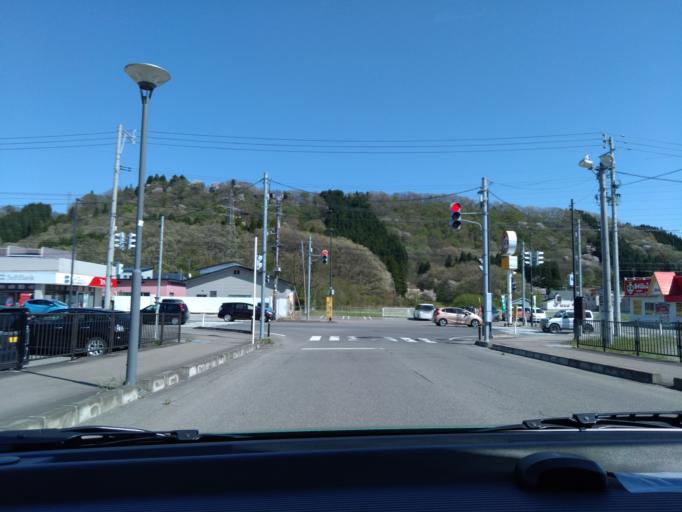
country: JP
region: Akita
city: Kakunodatemachi
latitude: 39.5906
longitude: 140.5736
